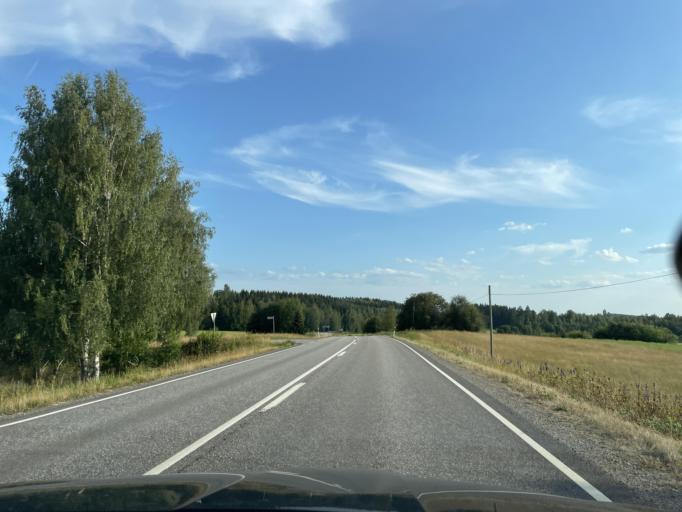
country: FI
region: Paijanne Tavastia
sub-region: Lahti
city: Auttoinen
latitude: 61.2964
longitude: 25.0878
